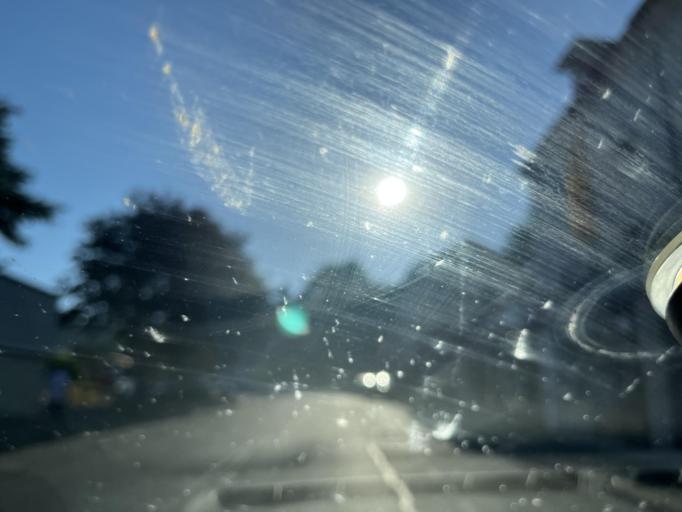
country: FR
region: Haute-Normandie
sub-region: Departement de la Seine-Maritime
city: Lillebonne
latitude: 49.5200
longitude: 0.5377
